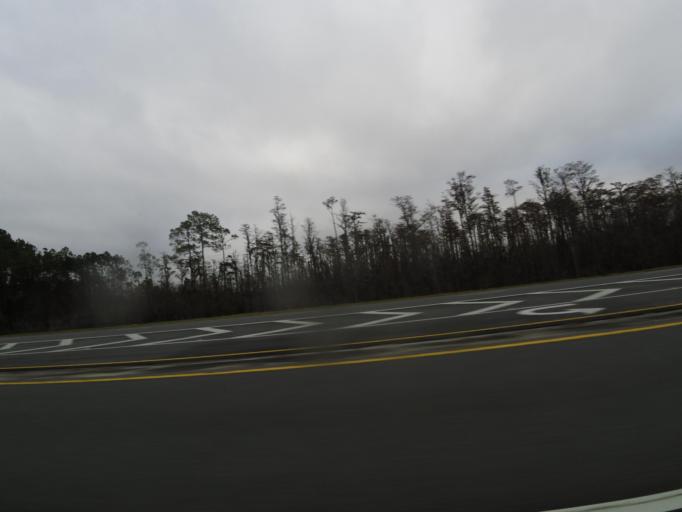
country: US
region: Georgia
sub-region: Charlton County
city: Folkston
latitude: 30.8763
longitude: -82.0295
